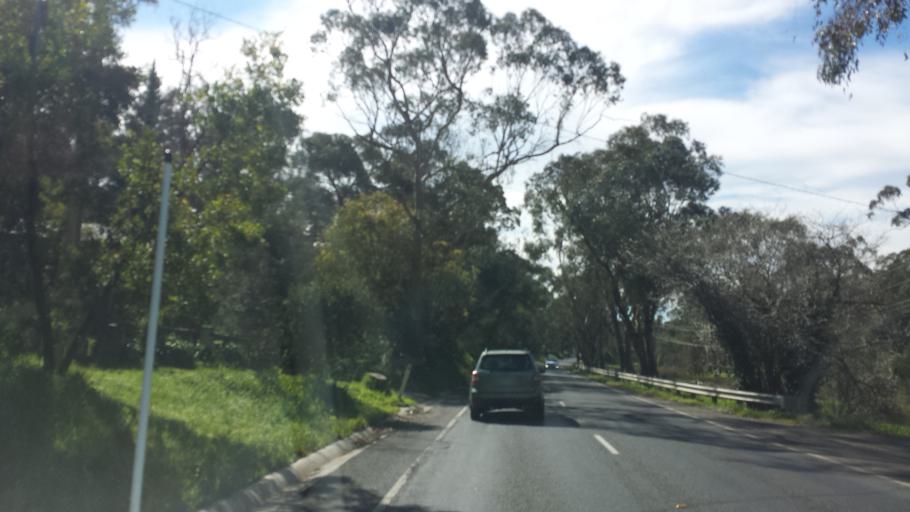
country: AU
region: Victoria
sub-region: Manningham
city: Warrandyte
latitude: -37.7515
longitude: 145.2346
